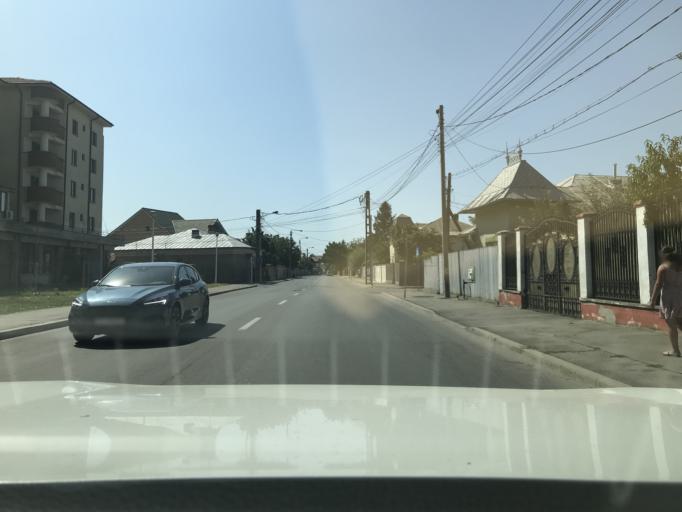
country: RO
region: Olt
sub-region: Municipiul Slatina
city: Slatina
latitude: 44.4234
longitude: 24.3619
